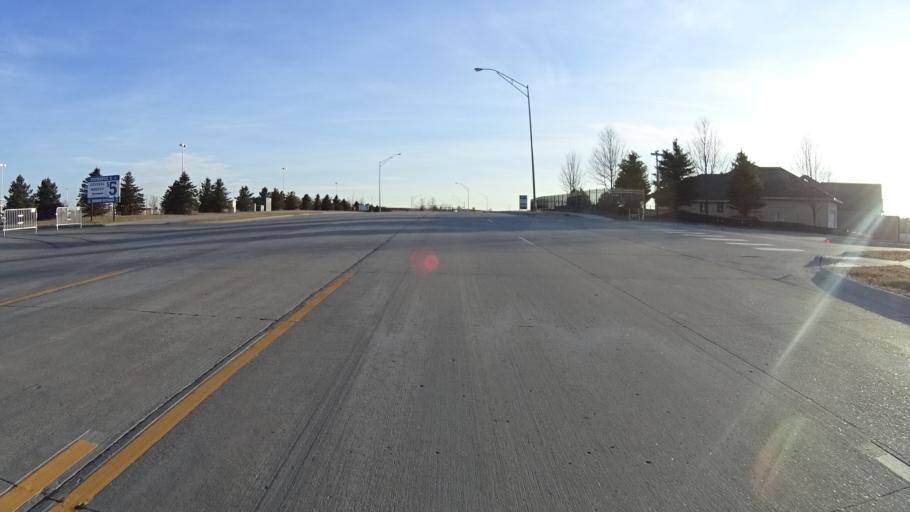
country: US
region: Nebraska
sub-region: Sarpy County
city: Chalco
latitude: 41.1525
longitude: -96.1099
